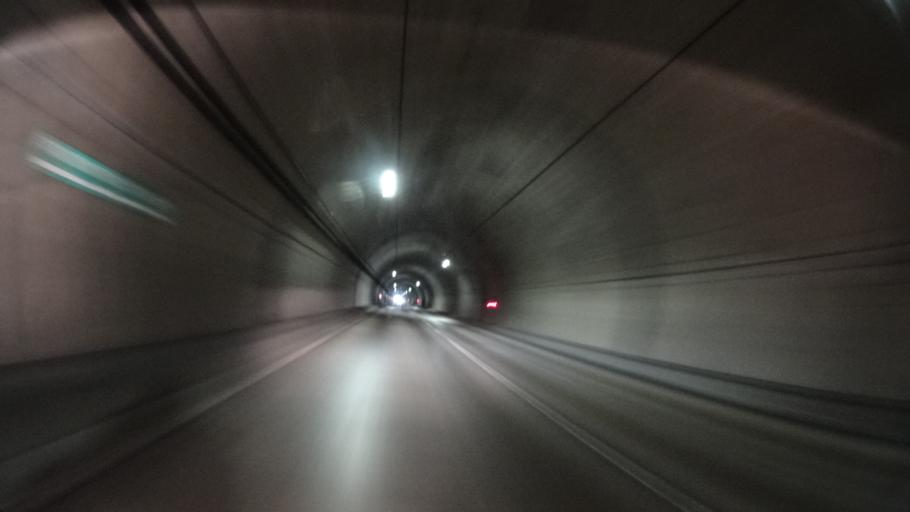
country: JP
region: Fukui
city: Maruoka
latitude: 36.1309
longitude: 136.3238
